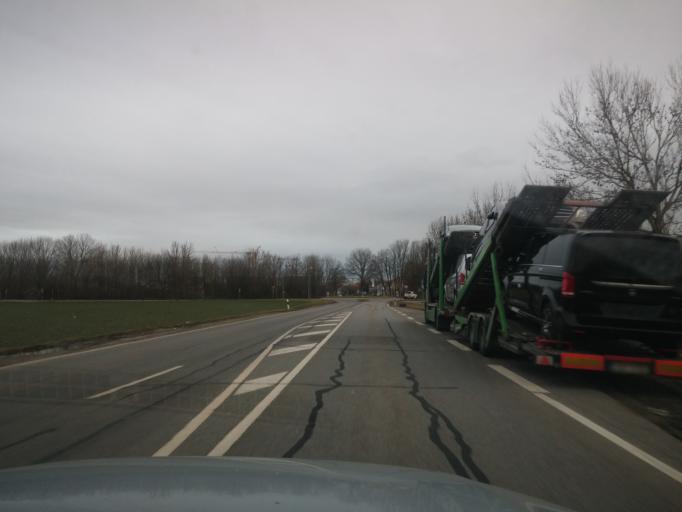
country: DE
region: Bavaria
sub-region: Upper Bavaria
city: Aschheim
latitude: 48.1823
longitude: 11.7092
